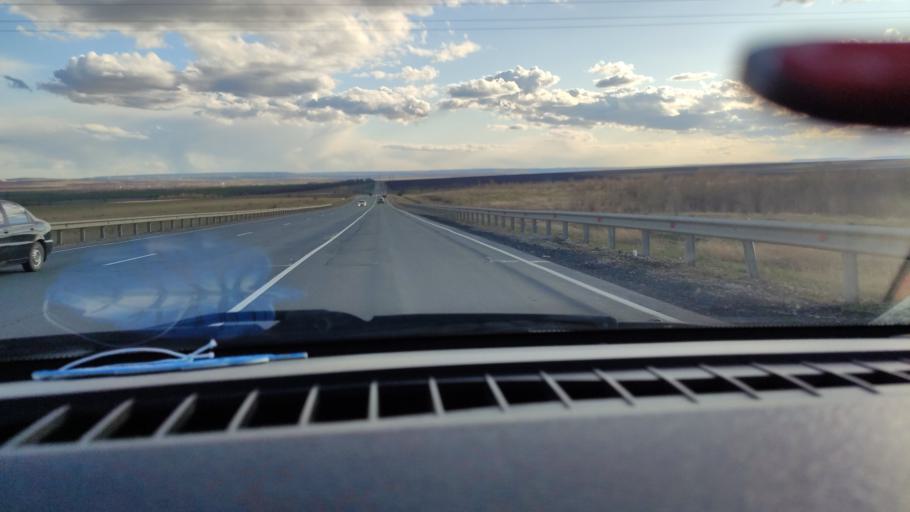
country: RU
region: Saratov
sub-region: Saratovskiy Rayon
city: Saratov
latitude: 51.7603
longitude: 46.0706
